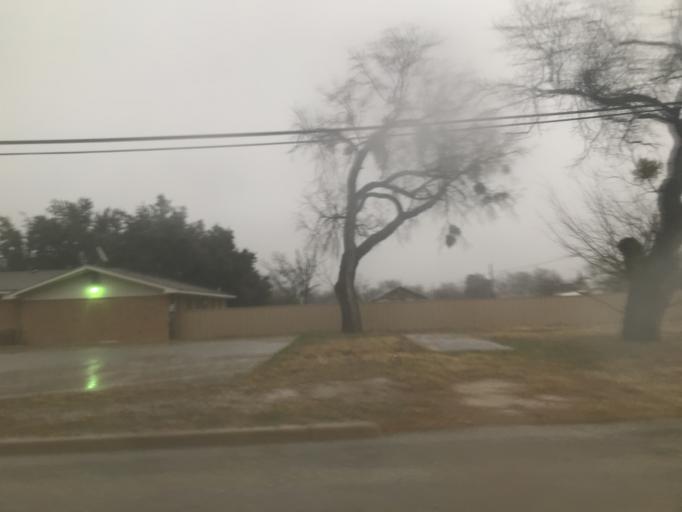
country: US
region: Texas
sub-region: Tom Green County
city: San Angelo
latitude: 31.4675
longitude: -100.4174
